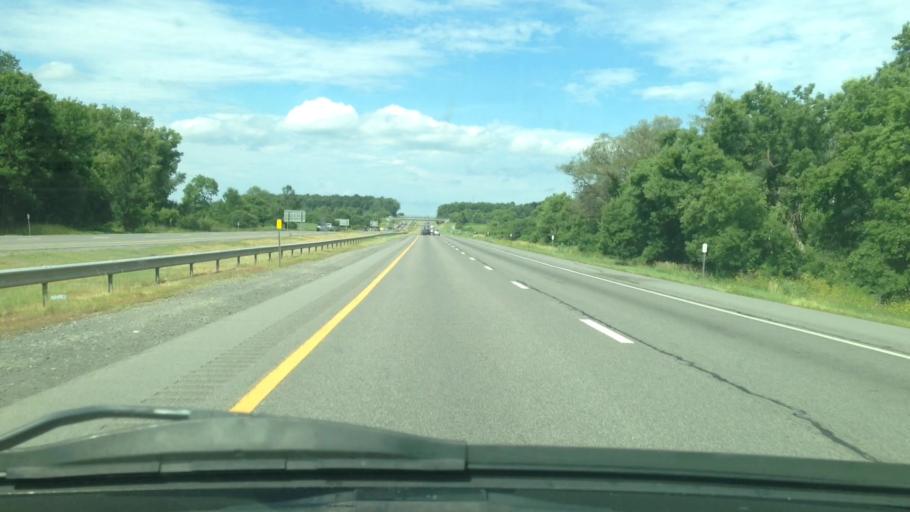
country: US
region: New York
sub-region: Cayuga County
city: Weedsport
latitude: 43.0596
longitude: -76.5727
